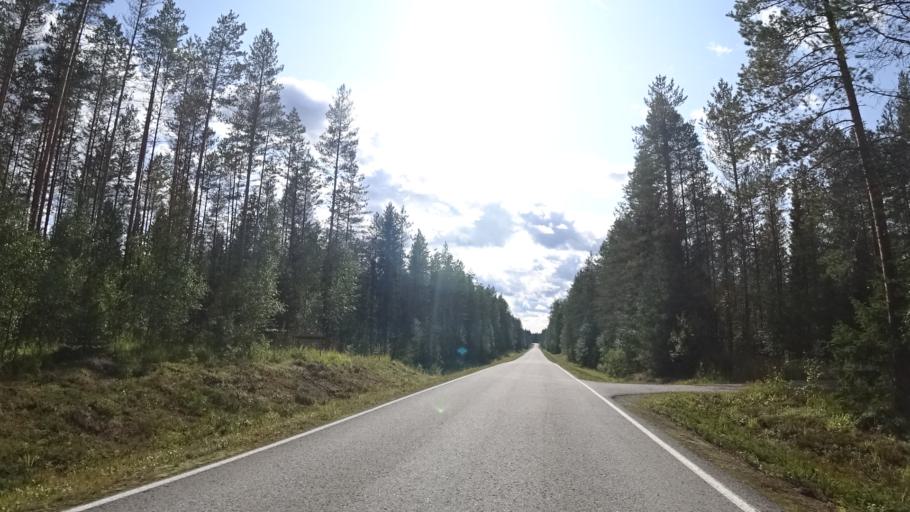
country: RU
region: Republic of Karelia
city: Vyartsilya
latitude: 62.2478
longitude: 30.7225
